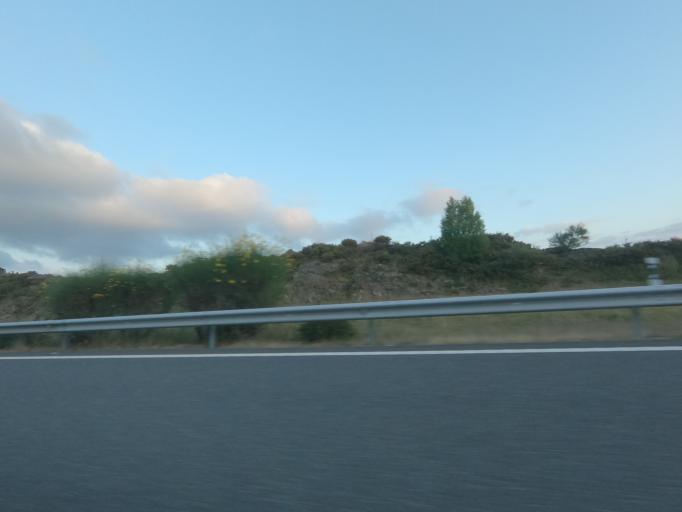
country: ES
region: Galicia
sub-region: Provincia de Pontevedra
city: Covelo
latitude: 42.1865
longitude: -8.3156
